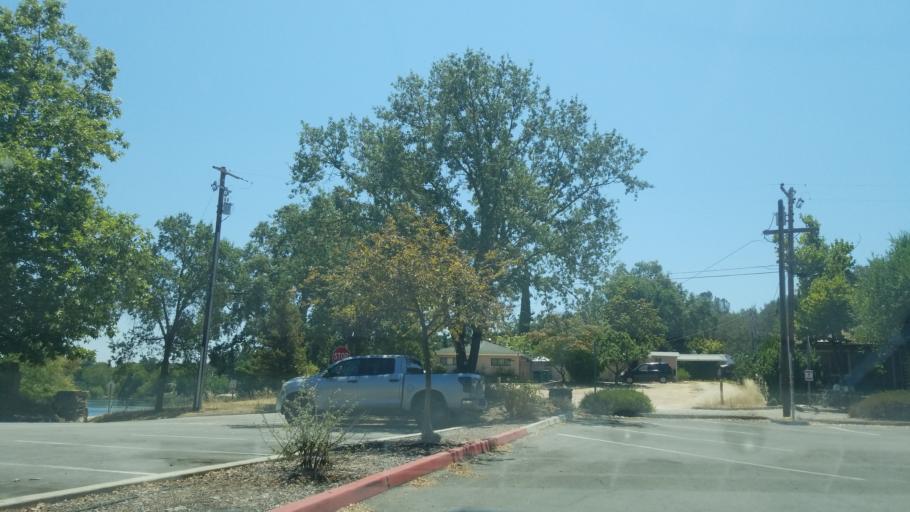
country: US
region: California
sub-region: San Luis Obispo County
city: Atascadero
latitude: 35.4660
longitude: -120.6688
